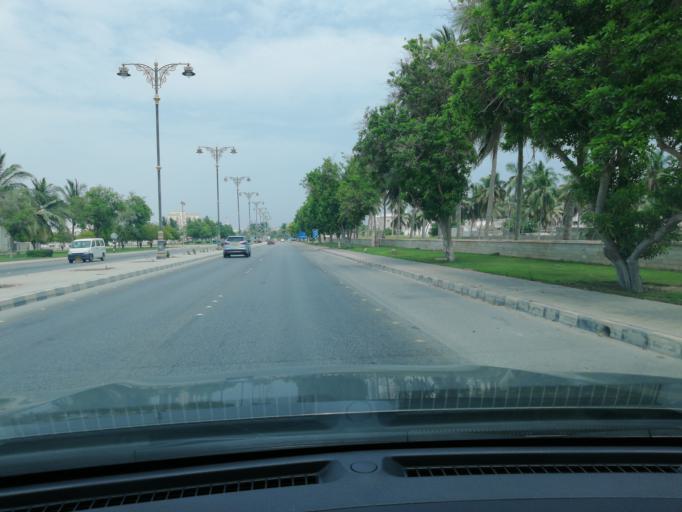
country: OM
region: Zufar
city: Salalah
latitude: 17.0043
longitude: 54.0551
